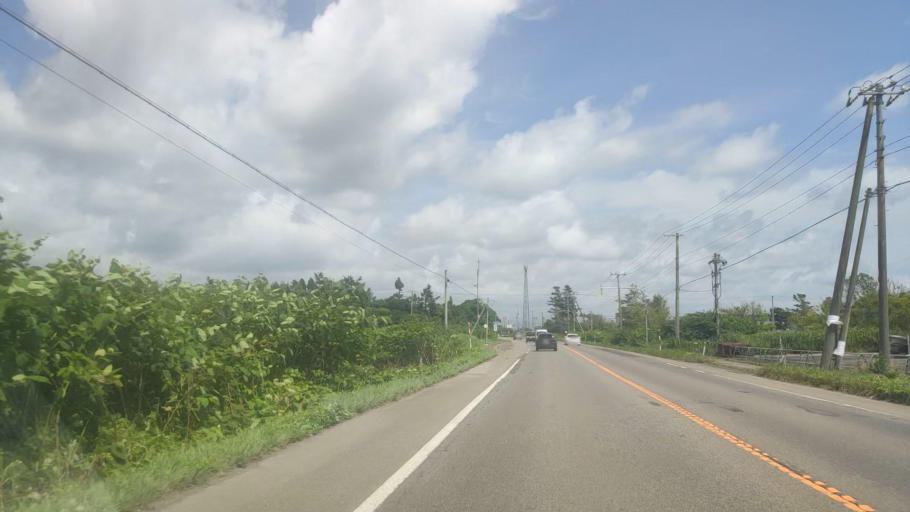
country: JP
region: Hokkaido
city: Niseko Town
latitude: 42.4695
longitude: 140.3425
